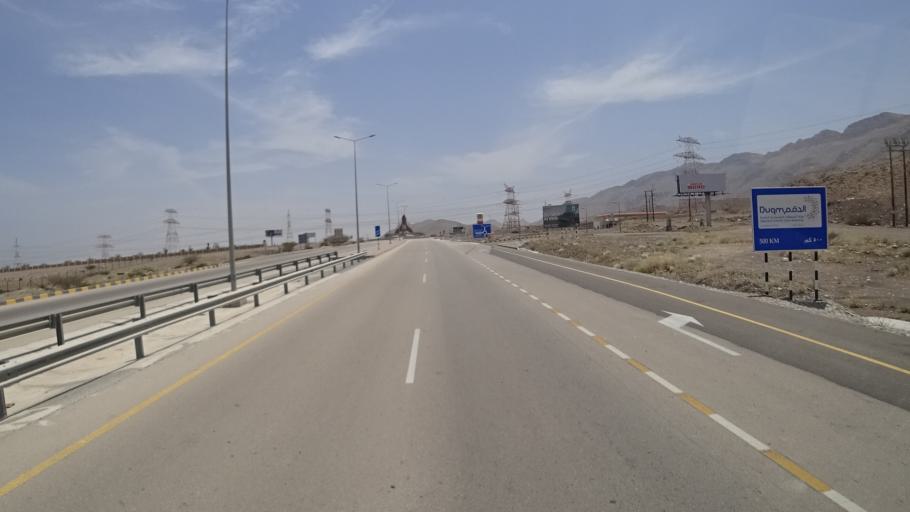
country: OM
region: Ash Sharqiyah
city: Sur
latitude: 22.6527
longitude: 59.3935
